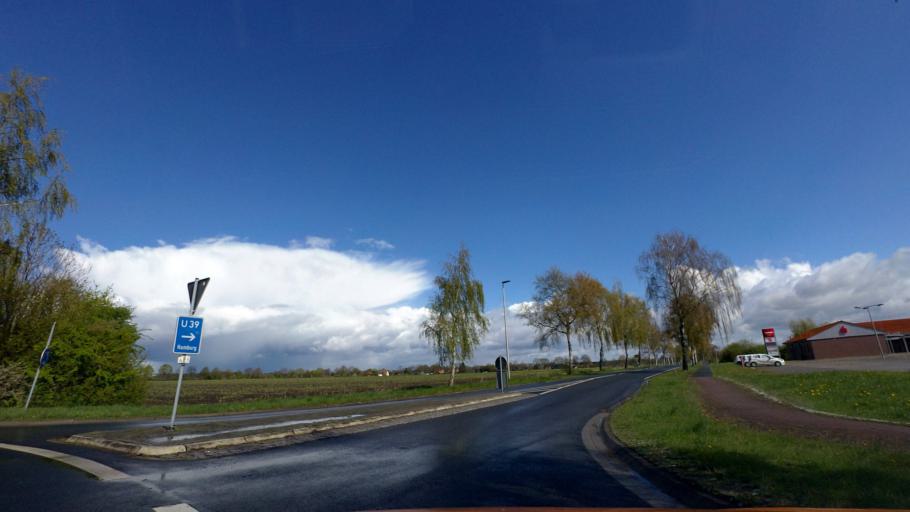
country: DE
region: Lower Saxony
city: Ottersberg
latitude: 53.0674
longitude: 9.0910
